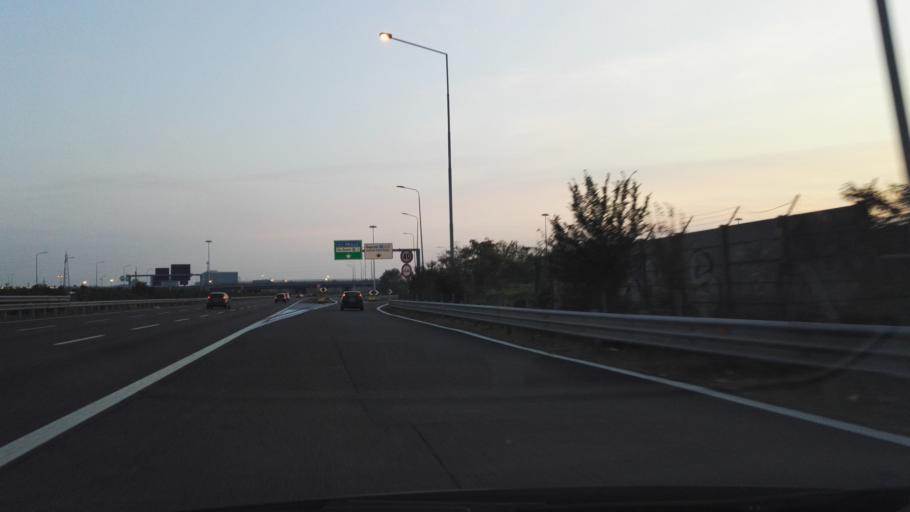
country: IT
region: Lombardy
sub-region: Citta metropolitana di Milano
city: Linate
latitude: 45.4391
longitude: 9.2564
